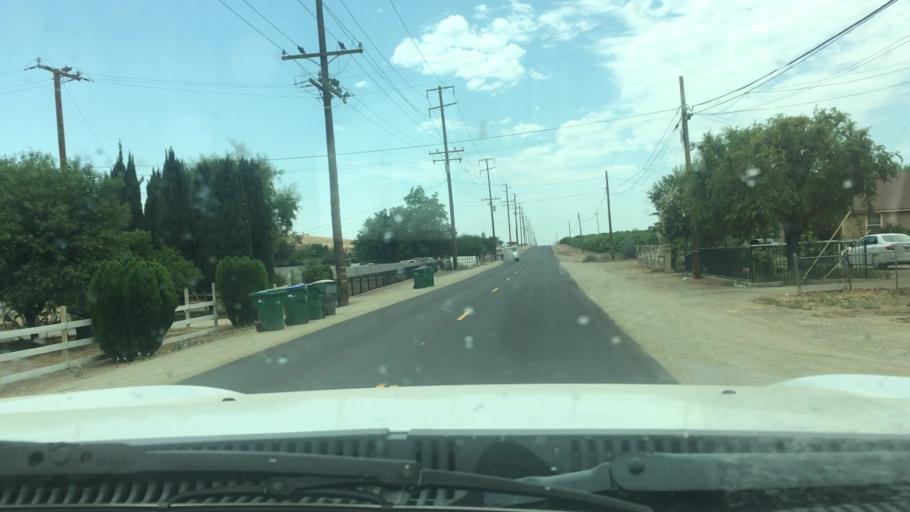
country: US
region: California
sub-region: Tulare County
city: Porterville
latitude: 36.0964
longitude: -119.0192
